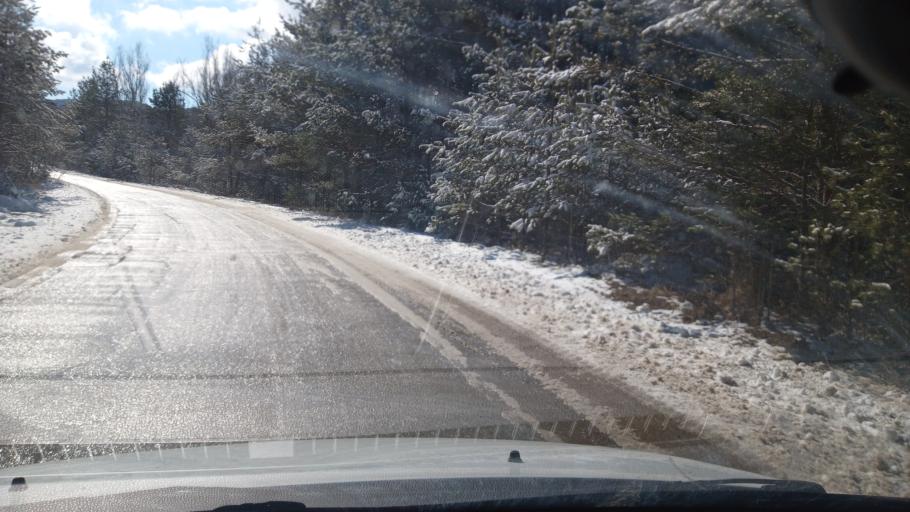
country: BG
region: Sofia-Capital
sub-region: Stolichna Obshtina
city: Sofia
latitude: 42.4889
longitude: 23.3823
